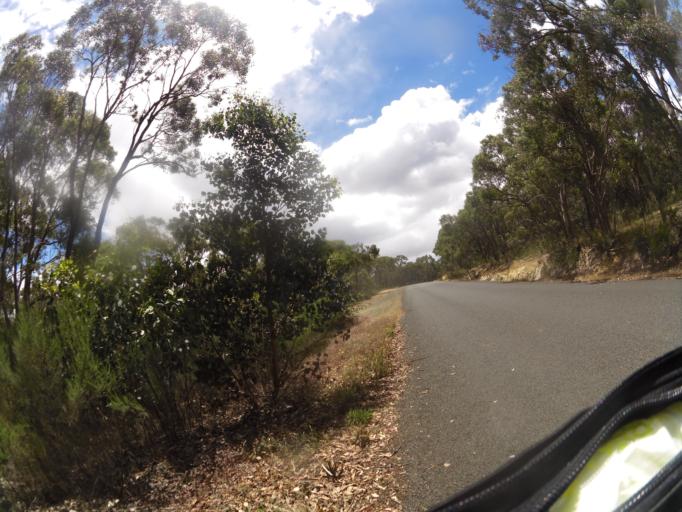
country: AU
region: Victoria
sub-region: Mount Alexander
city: Castlemaine
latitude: -37.0228
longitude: 144.2424
